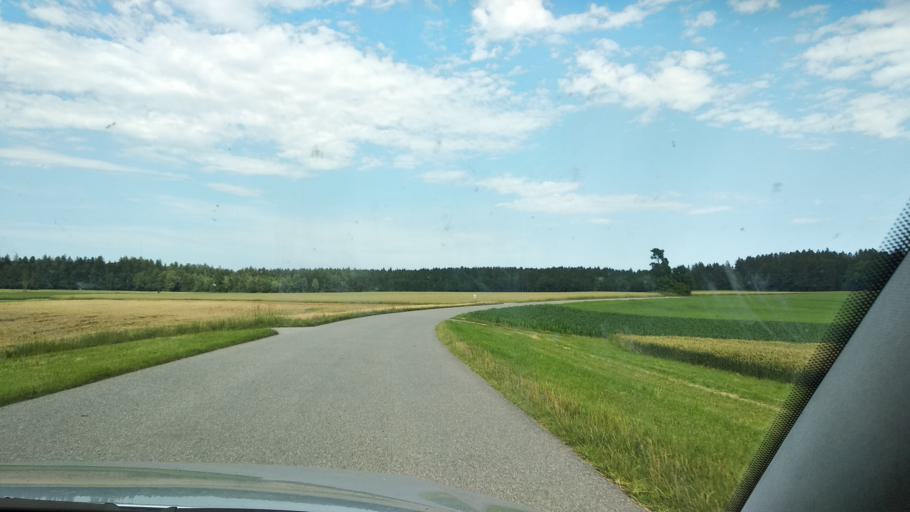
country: DE
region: Bavaria
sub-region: Upper Bavaria
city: Kirchseeon
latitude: 48.0519
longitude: 11.9009
